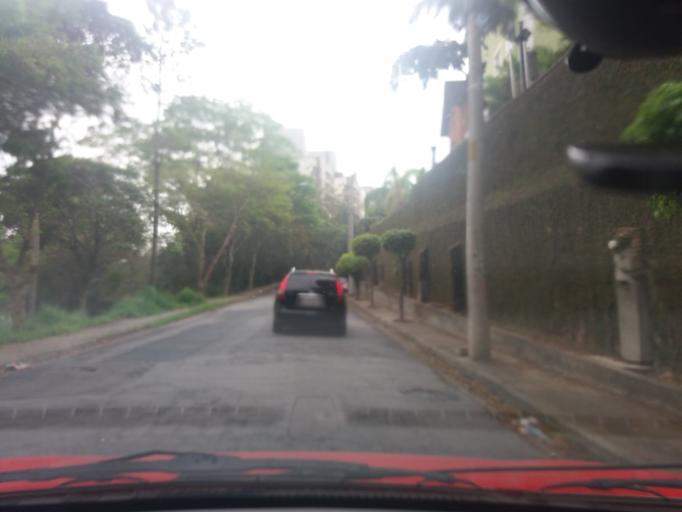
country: BR
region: Sao Paulo
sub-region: Taboao Da Serra
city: Taboao da Serra
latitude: -23.6032
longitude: -46.7260
